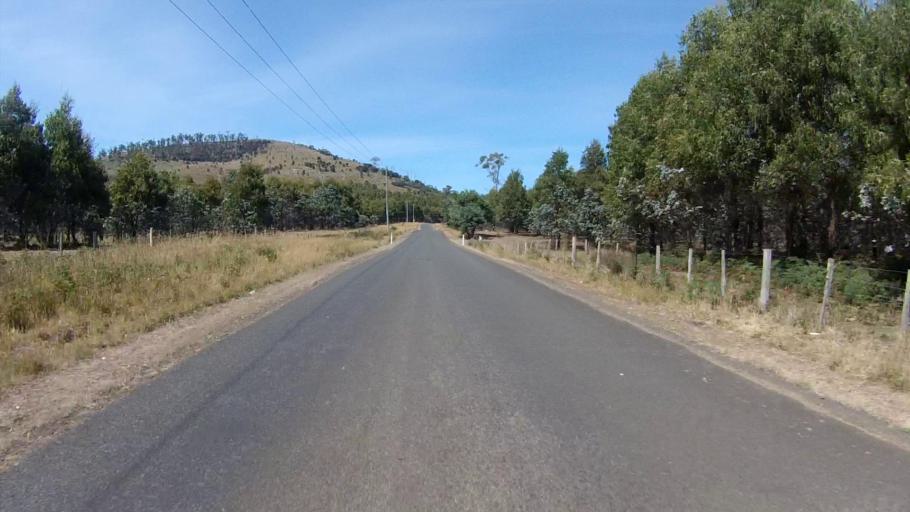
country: AU
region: Tasmania
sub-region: Sorell
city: Sorell
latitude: -42.6222
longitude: 147.7294
